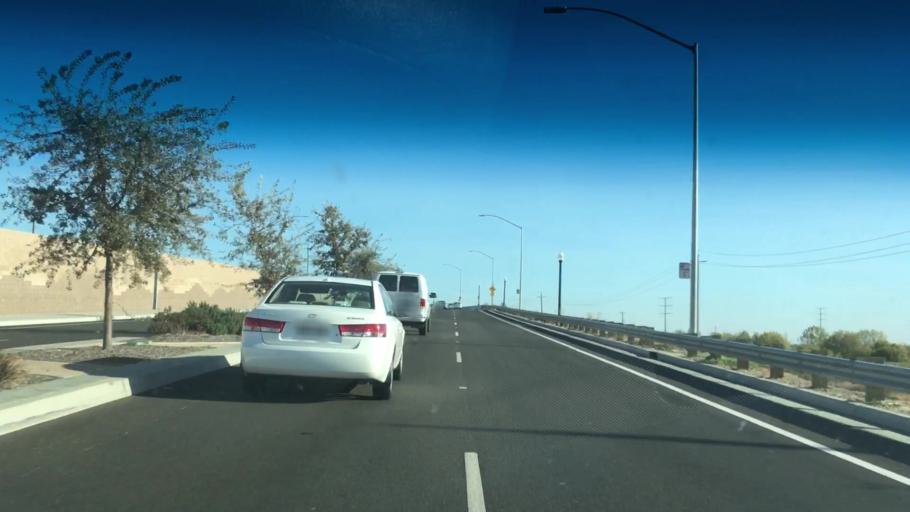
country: US
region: California
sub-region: Sacramento County
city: Parkway
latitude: 38.4624
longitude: -121.4639
